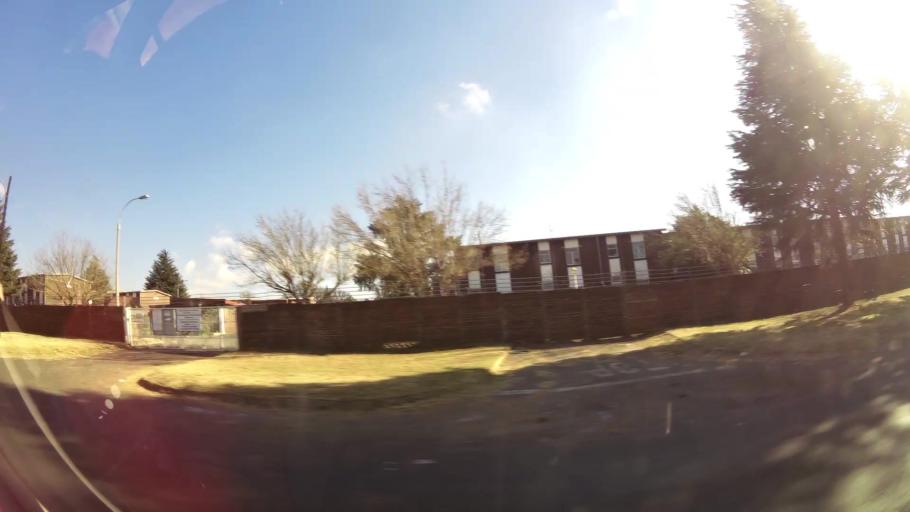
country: ZA
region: Gauteng
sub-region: City of Johannesburg Metropolitan Municipality
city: Roodepoort
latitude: -26.1525
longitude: 27.8346
